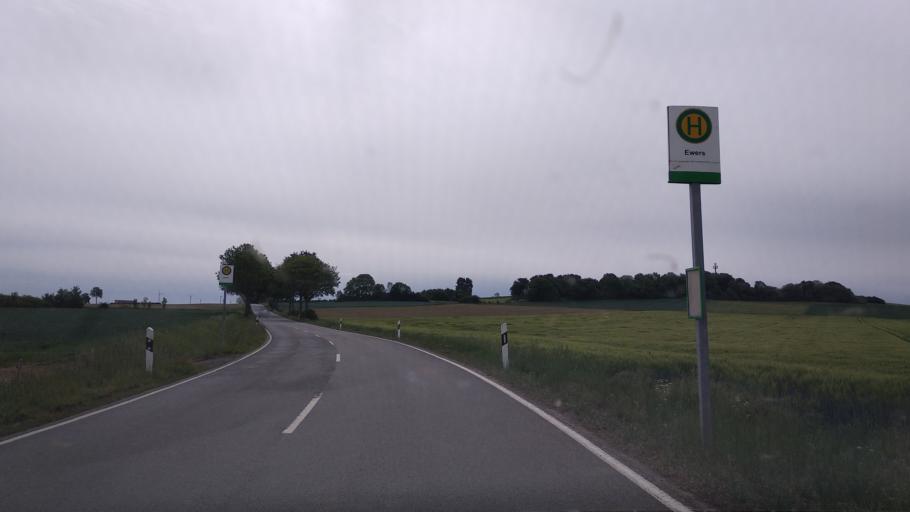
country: DE
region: North Rhine-Westphalia
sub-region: Regierungsbezirk Detmold
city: Willebadessen
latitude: 51.6121
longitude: 9.1062
